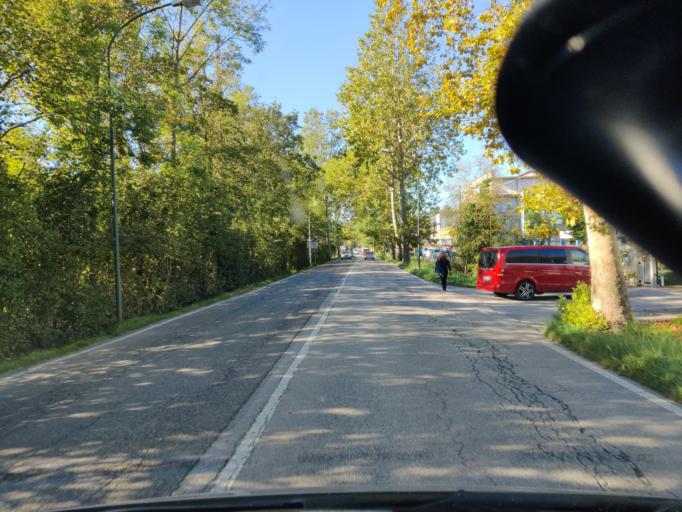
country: IT
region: Veneto
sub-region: Provincia di Belluno
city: Belluno
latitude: 46.1620
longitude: 12.2405
